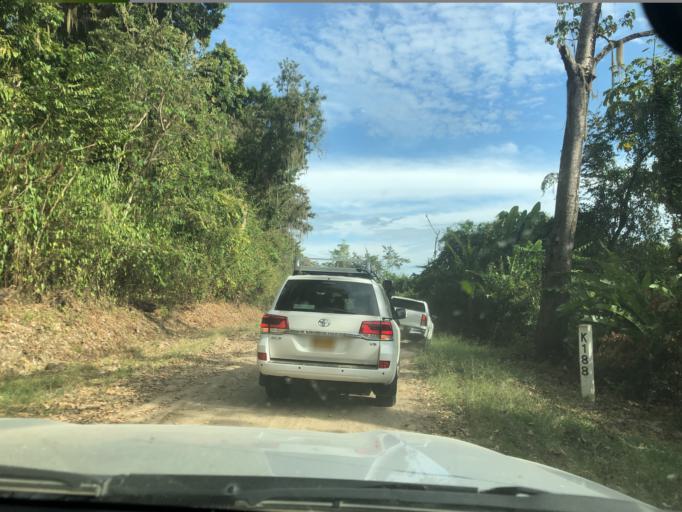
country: CR
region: Alajuela
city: San Jose
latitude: 11.1230
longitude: -85.2887
